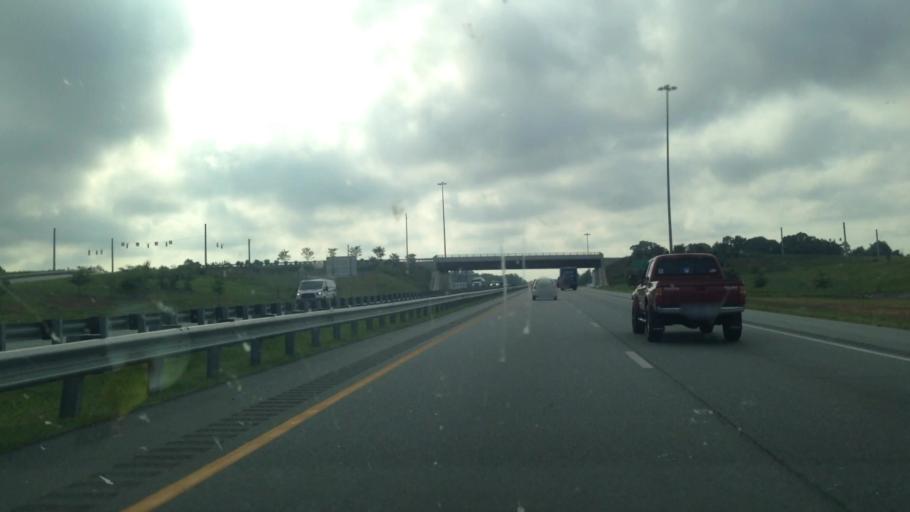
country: US
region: North Carolina
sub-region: Forsyth County
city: Kernersville
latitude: 36.1071
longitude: -80.0490
